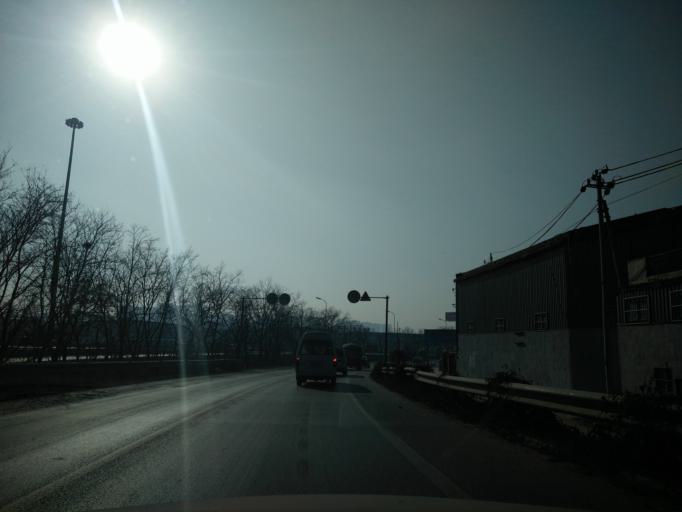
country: CN
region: Beijing
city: Jiugong
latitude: 39.8182
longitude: 116.4954
